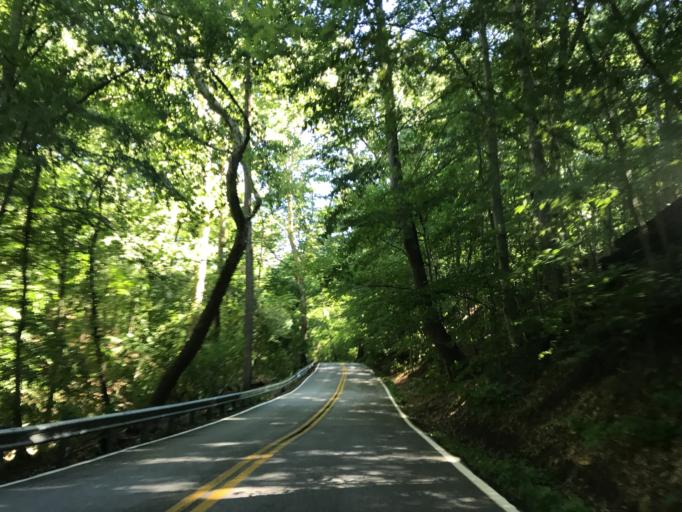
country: US
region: Maryland
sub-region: Howard County
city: Ilchester
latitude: 39.2562
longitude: -76.7658
